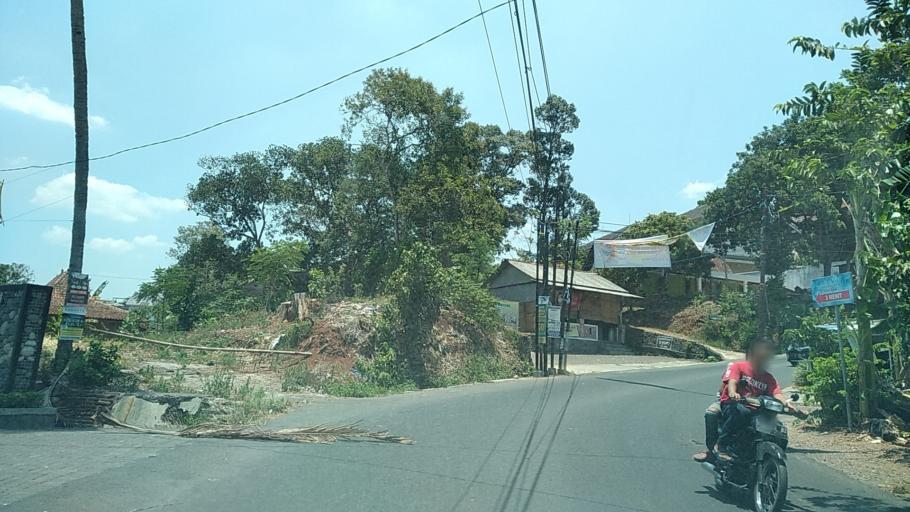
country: ID
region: Central Java
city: Ungaran
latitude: -7.0769
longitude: 110.4213
